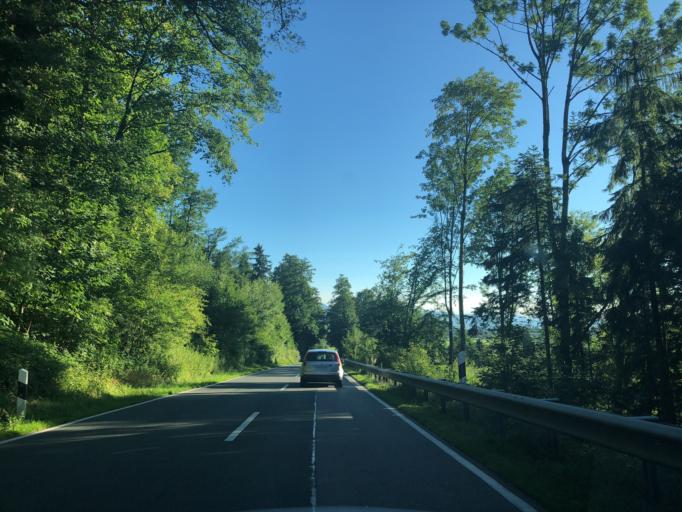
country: DE
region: Bavaria
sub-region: Upper Bavaria
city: Riedering
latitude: 47.8472
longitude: 12.2212
